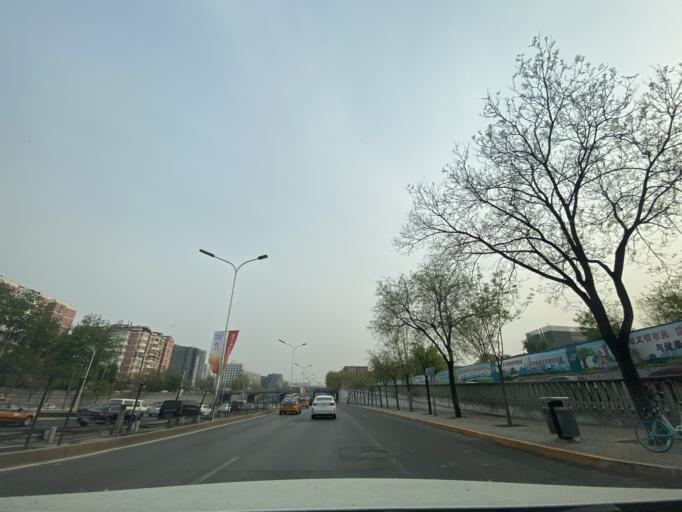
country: CN
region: Beijing
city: Sijiqing
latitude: 39.9350
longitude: 116.2680
